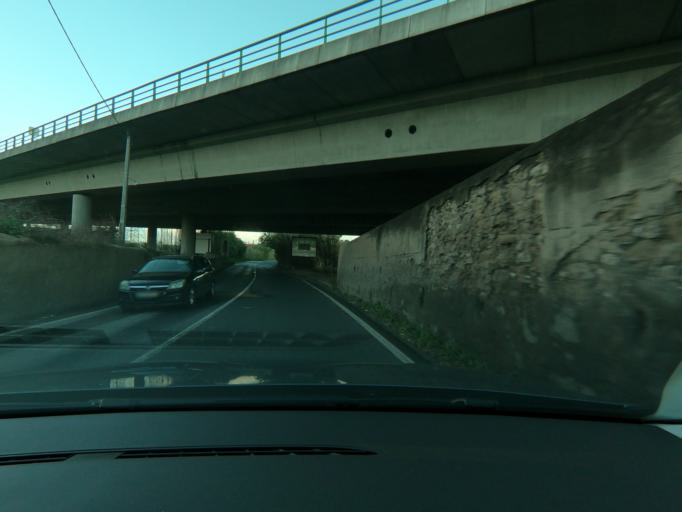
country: PT
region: Lisbon
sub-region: Alenquer
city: Carregado
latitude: 39.0184
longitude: -8.9738
